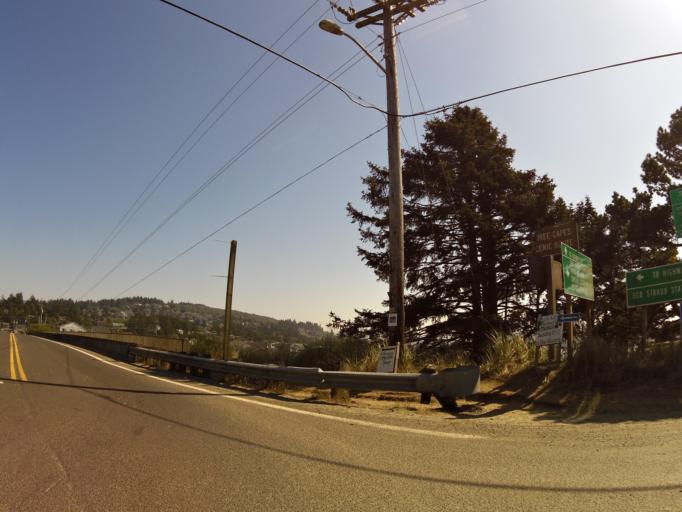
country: US
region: Oregon
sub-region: Tillamook County
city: Pacific City
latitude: 45.2023
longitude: -123.9660
